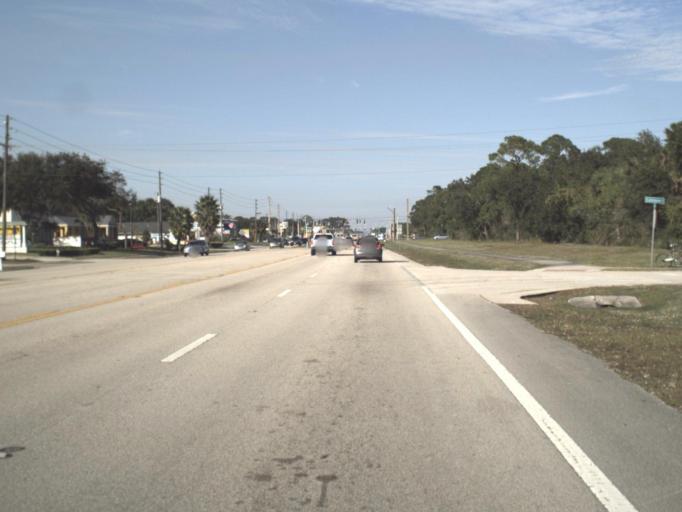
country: US
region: Florida
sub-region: Brevard County
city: June Park
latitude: 28.0294
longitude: -80.6715
